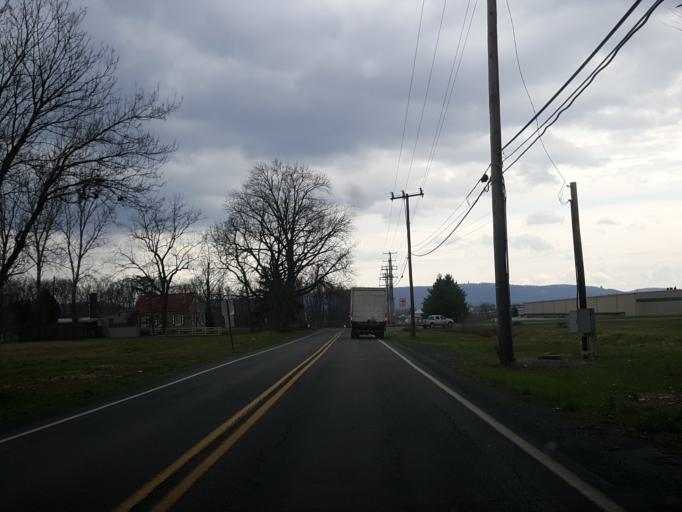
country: US
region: Pennsylvania
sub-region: Berks County
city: Fox Chase
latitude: 40.3884
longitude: -75.9791
